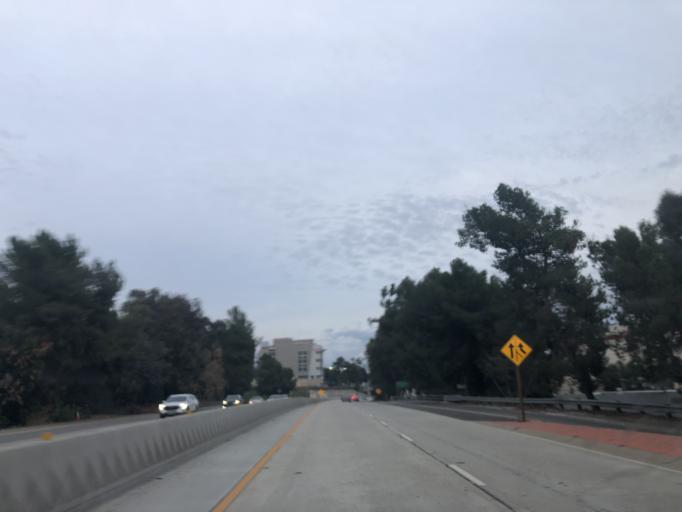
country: US
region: California
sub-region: Los Angeles County
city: Glendale
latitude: 34.1415
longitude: -118.2743
